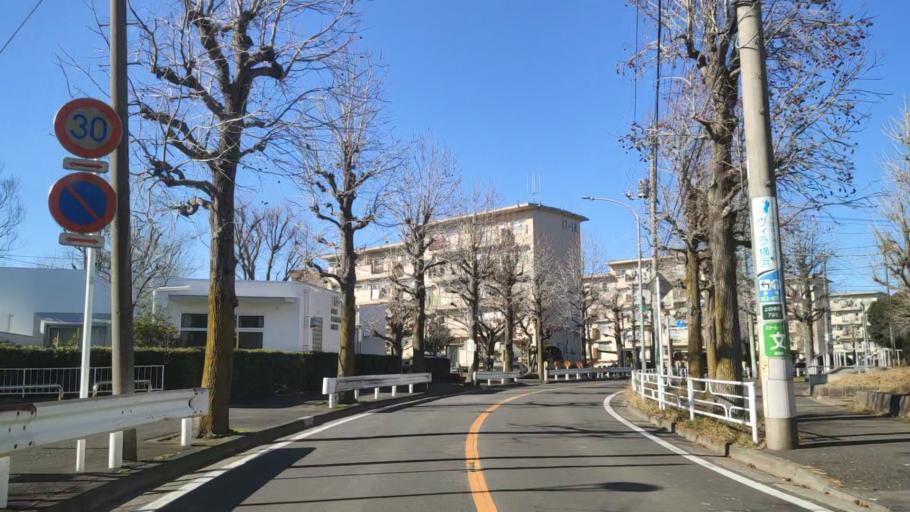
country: JP
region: Kanagawa
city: Minami-rinkan
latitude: 35.4993
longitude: 139.5304
